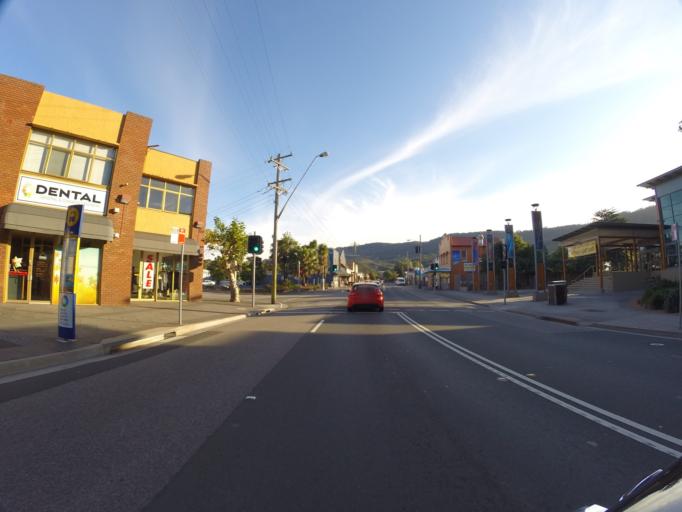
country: AU
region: New South Wales
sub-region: Wollongong
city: Bulli
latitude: -34.3172
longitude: 150.9187
